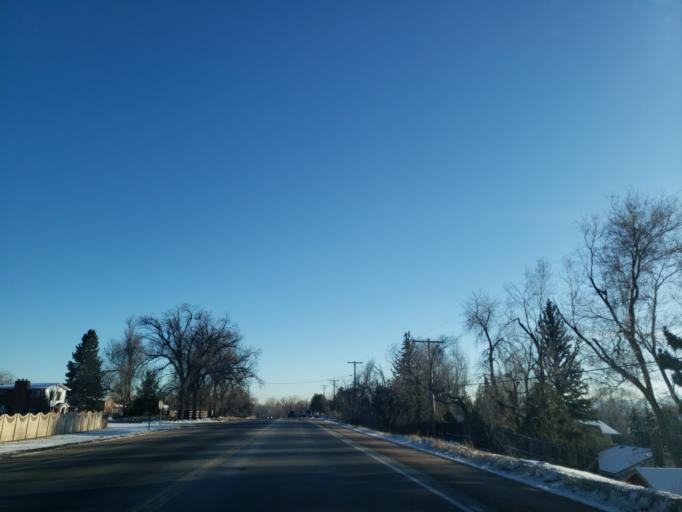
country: US
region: Colorado
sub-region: Larimer County
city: Fort Collins
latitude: 40.6358
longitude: -105.0723
